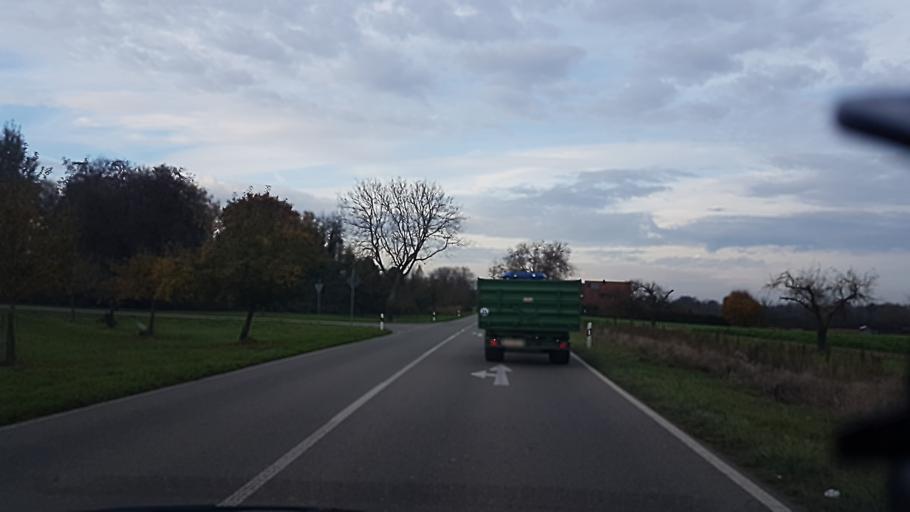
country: DE
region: Baden-Wuerttemberg
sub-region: Freiburg Region
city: Weisweil
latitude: 48.2057
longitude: 7.6840
